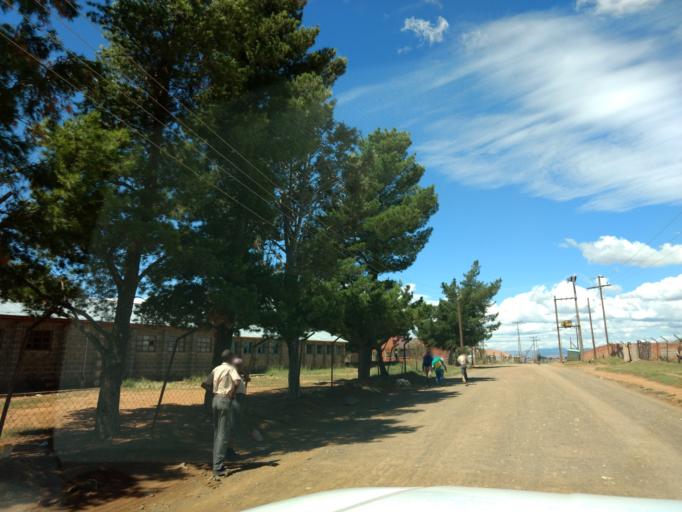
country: LS
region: Maseru
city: Maseru
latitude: -29.3724
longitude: 27.5089
